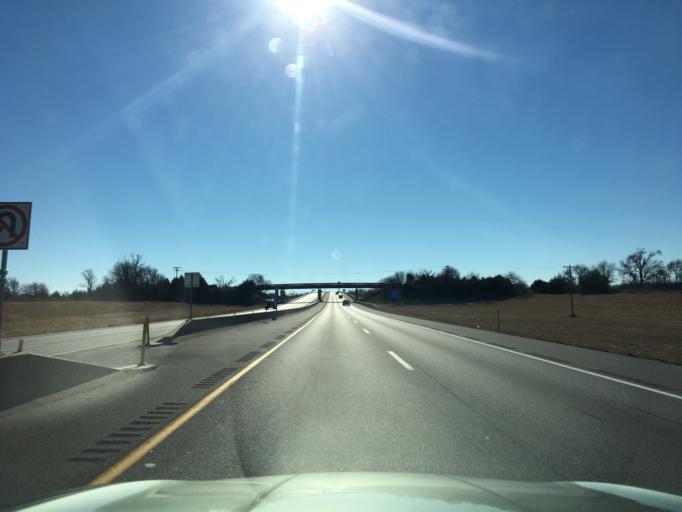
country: US
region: Kansas
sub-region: Sumner County
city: Belle Plaine
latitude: 37.3799
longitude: -97.3239
